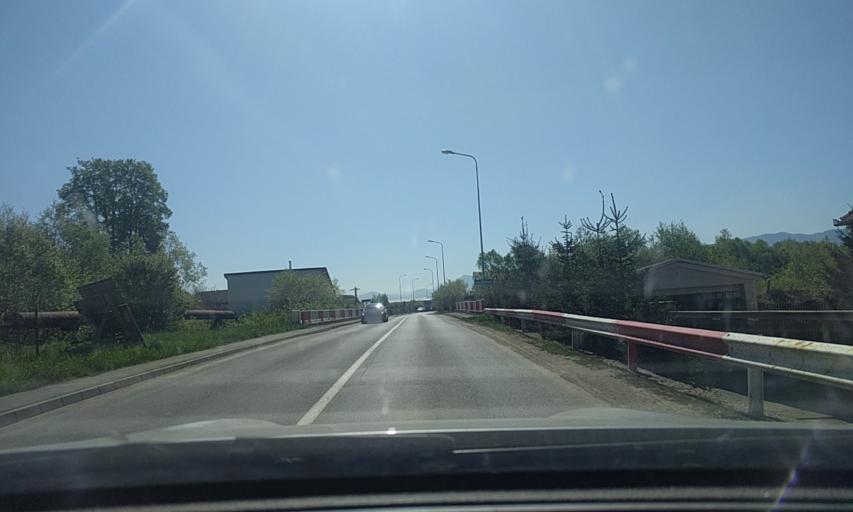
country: RO
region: Brasov
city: Brasov
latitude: 45.6918
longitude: 25.5646
